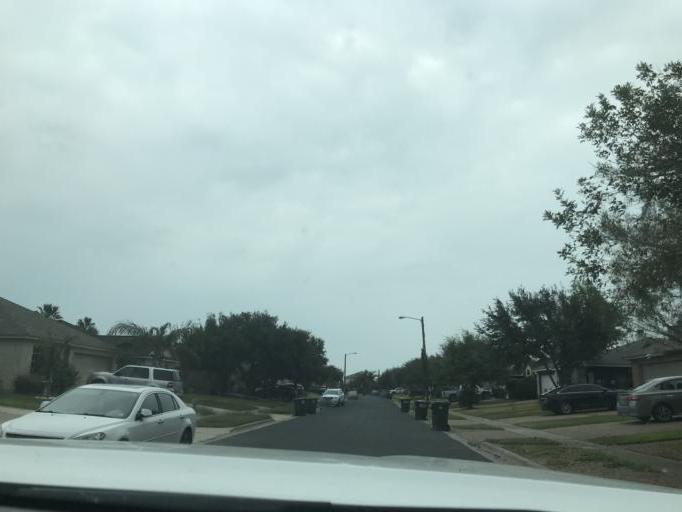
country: US
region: Texas
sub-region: Nueces County
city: Corpus Christi
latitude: 27.6671
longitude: -97.3443
